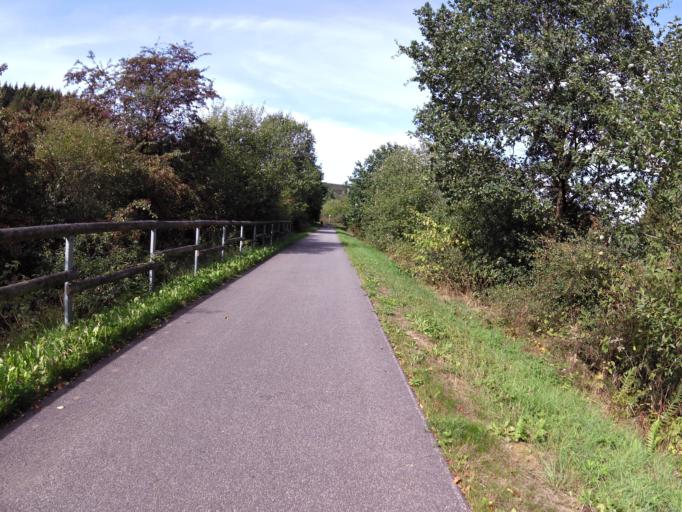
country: DE
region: Rheinland-Pfalz
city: Lunebach
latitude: 50.1471
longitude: 6.3371
